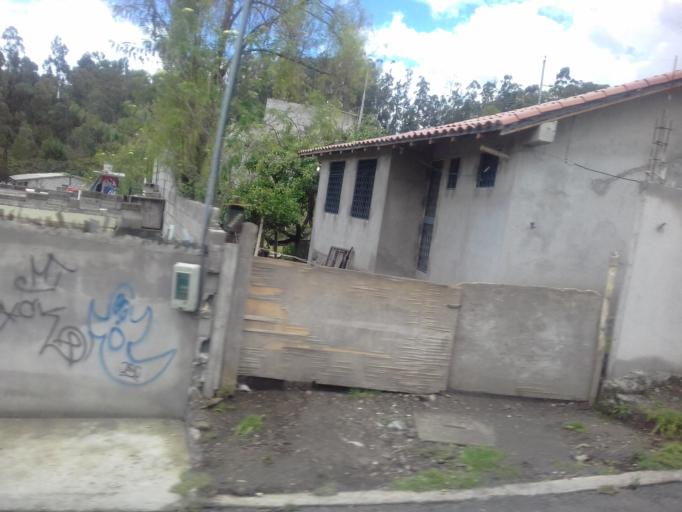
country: EC
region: Pichincha
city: Sangolqui
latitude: -0.3312
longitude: -78.4178
